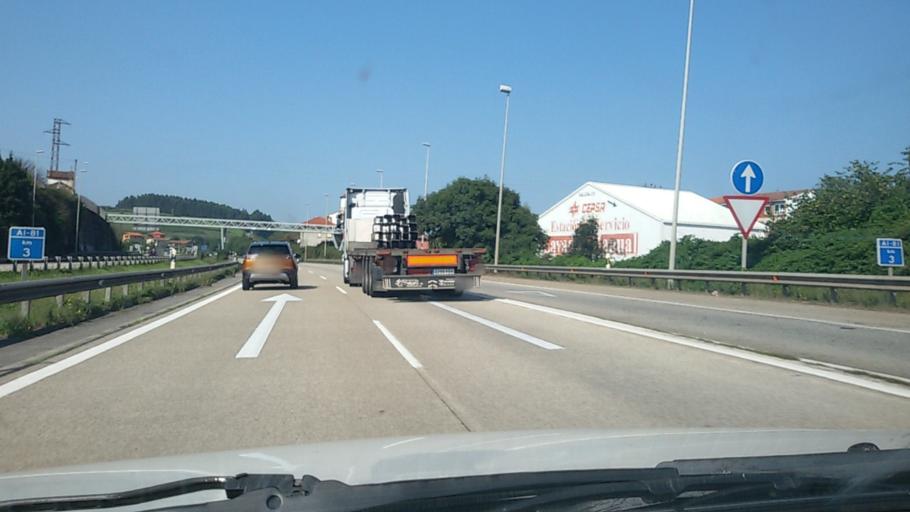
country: ES
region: Asturias
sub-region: Province of Asturias
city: Corvera de Asturias
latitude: 43.5501
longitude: -5.8721
